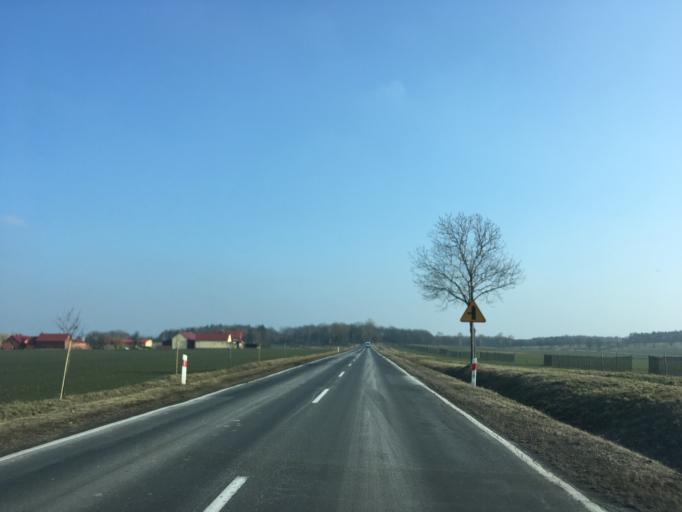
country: PL
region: Lower Silesian Voivodeship
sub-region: Powiat zlotoryjski
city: Olszanica
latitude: 51.2771
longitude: 15.8372
